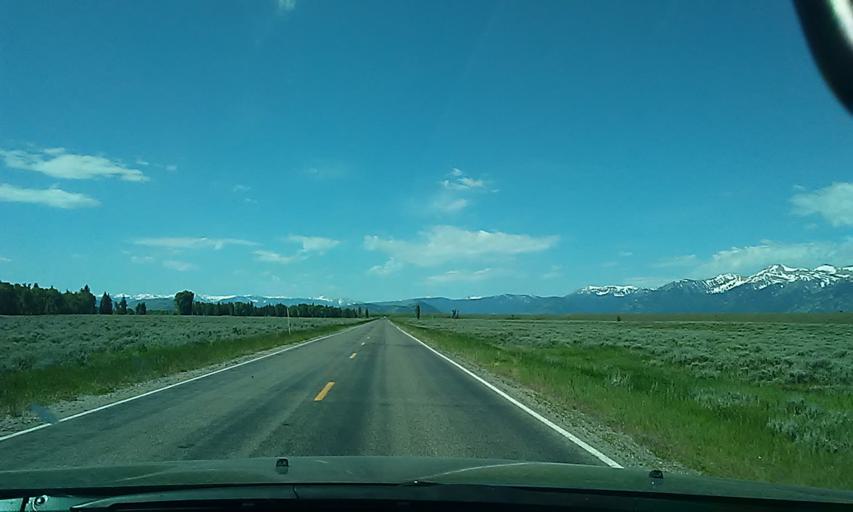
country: US
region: Wyoming
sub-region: Teton County
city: Jackson
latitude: 43.6142
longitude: -110.6792
